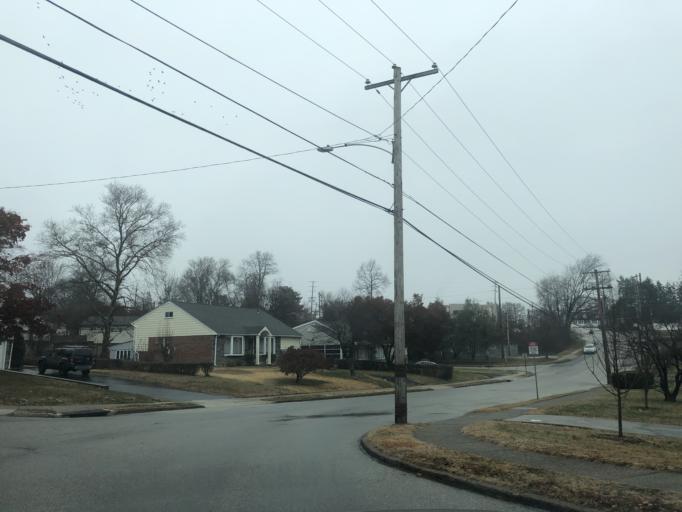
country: US
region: Pennsylvania
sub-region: Delaware County
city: Broomall
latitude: 39.9783
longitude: -75.3480
